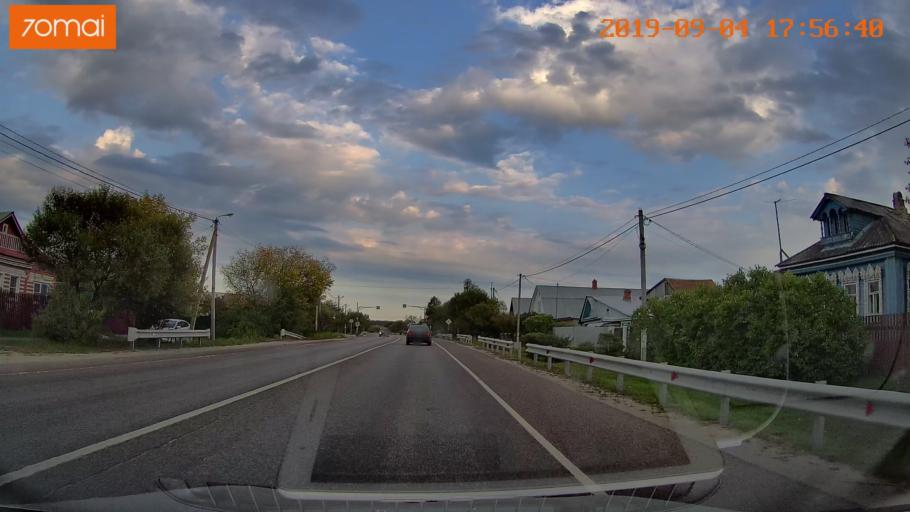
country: RU
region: Moskovskaya
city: Il'inskiy Pogost
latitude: 55.5038
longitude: 38.7822
